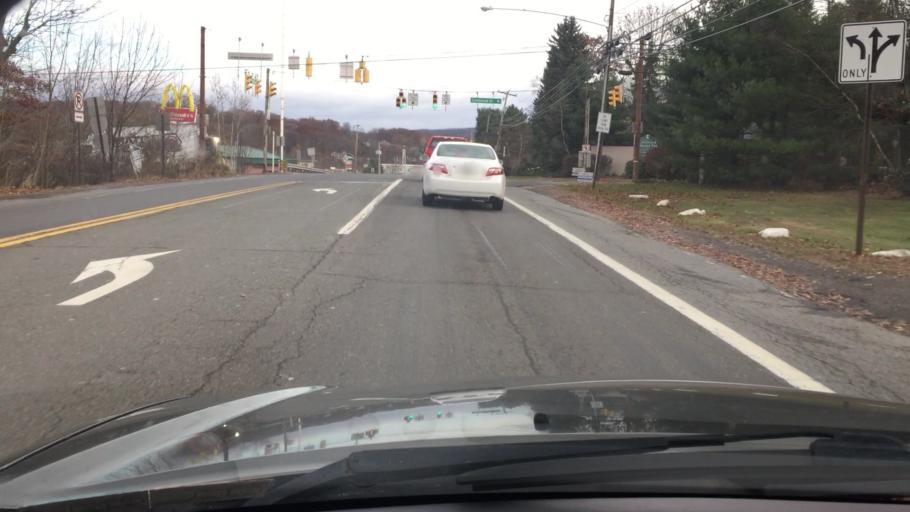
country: US
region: Pennsylvania
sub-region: Luzerne County
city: Mountain Top
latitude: 41.1426
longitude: -75.9003
